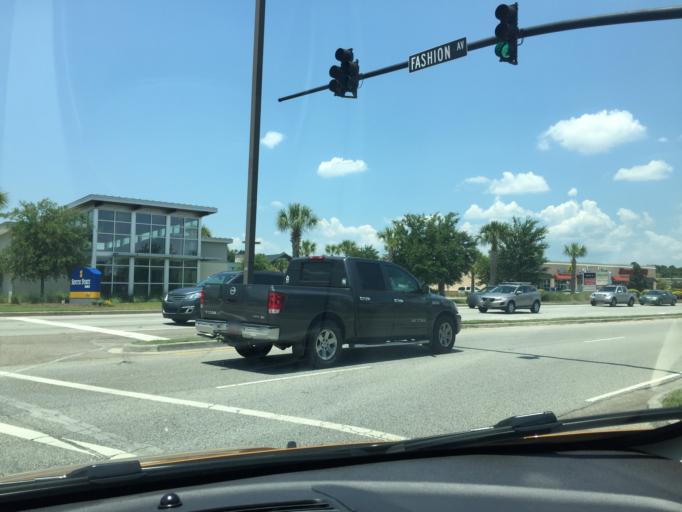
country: US
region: South Carolina
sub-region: Berkeley County
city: Hanahan
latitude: 32.8725
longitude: -80.0209
